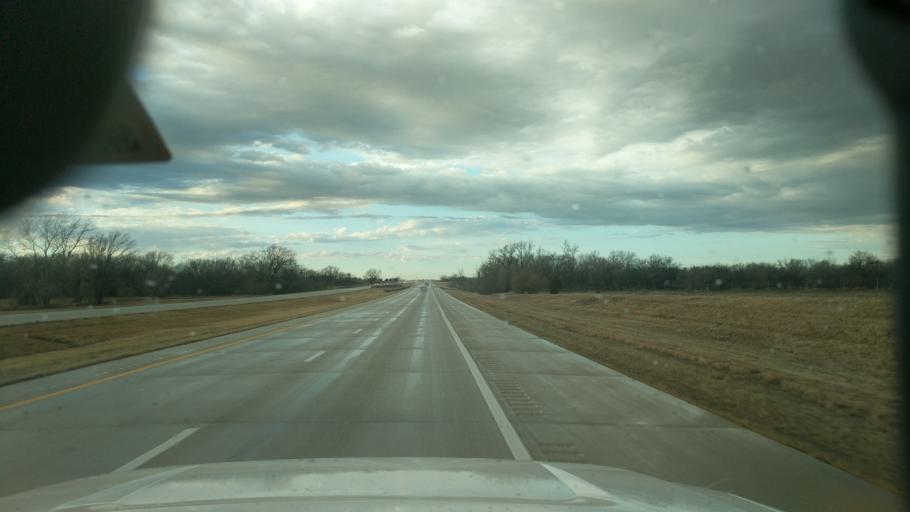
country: US
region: Kansas
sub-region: Harvey County
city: North Newton
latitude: 38.1057
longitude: -97.3762
